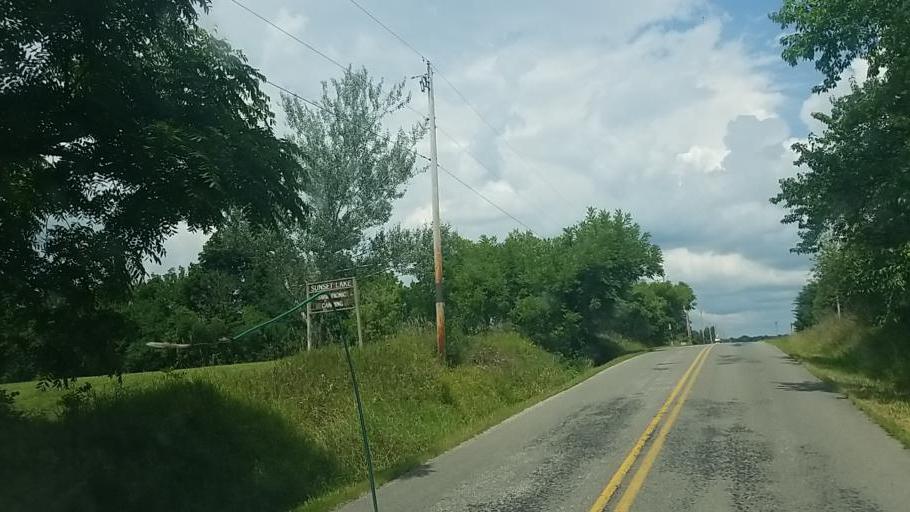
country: US
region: Ohio
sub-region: Medina County
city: Lodi
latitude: 41.1245
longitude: -82.0746
